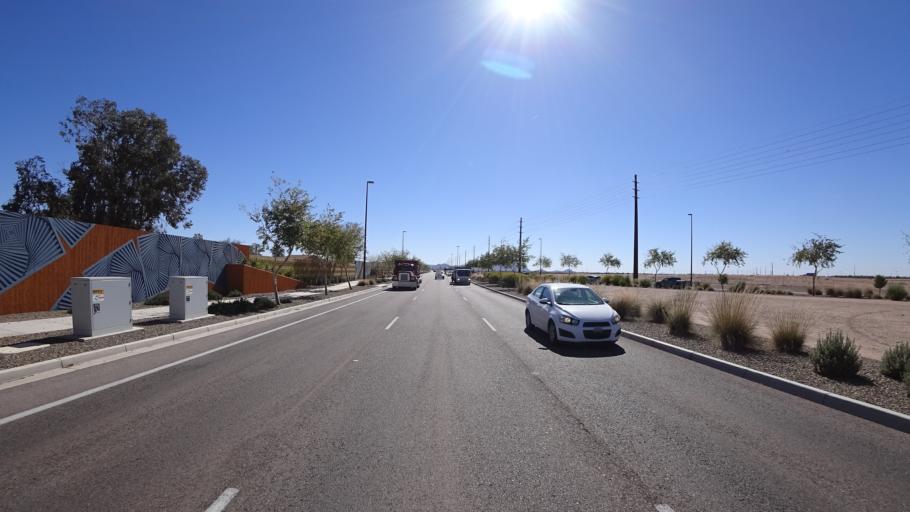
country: US
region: Arizona
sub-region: Maricopa County
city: Queen Creek
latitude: 33.3021
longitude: -111.6867
